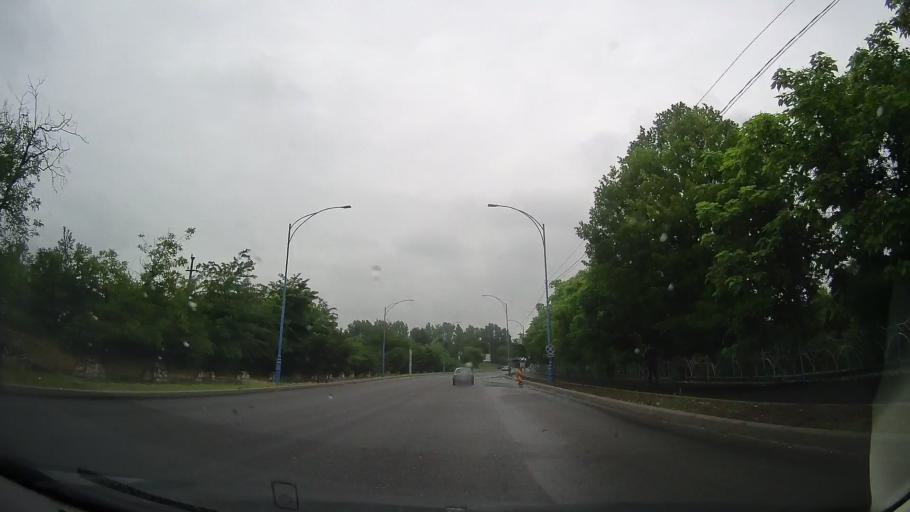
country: RO
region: Mehedinti
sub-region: Municipiul Drobeta-Turnu Severin
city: Drobeta-Turnu Severin
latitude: 44.6275
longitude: 22.6387
